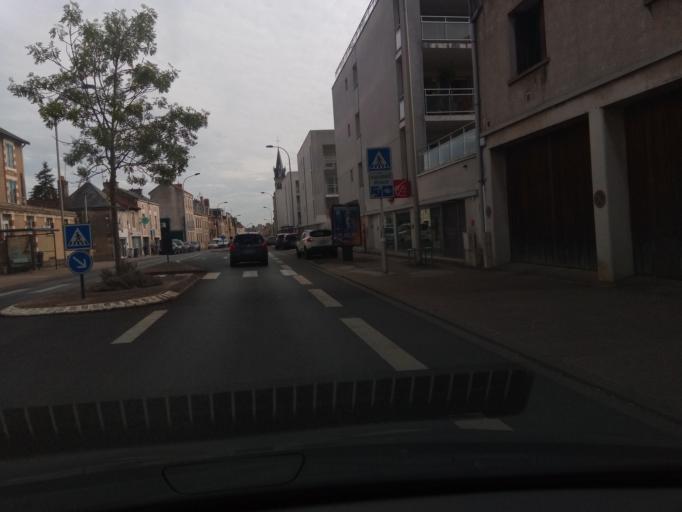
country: FR
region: Poitou-Charentes
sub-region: Departement de la Vienne
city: Biard
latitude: 46.5688
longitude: 0.3216
